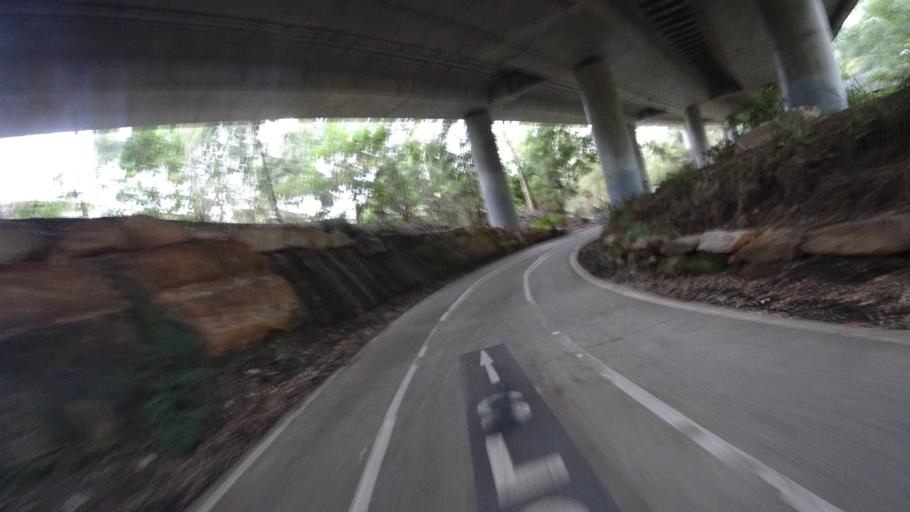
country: AU
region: New South Wales
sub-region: North Sydney
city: St Leonards
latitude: -33.8129
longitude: 151.1978
